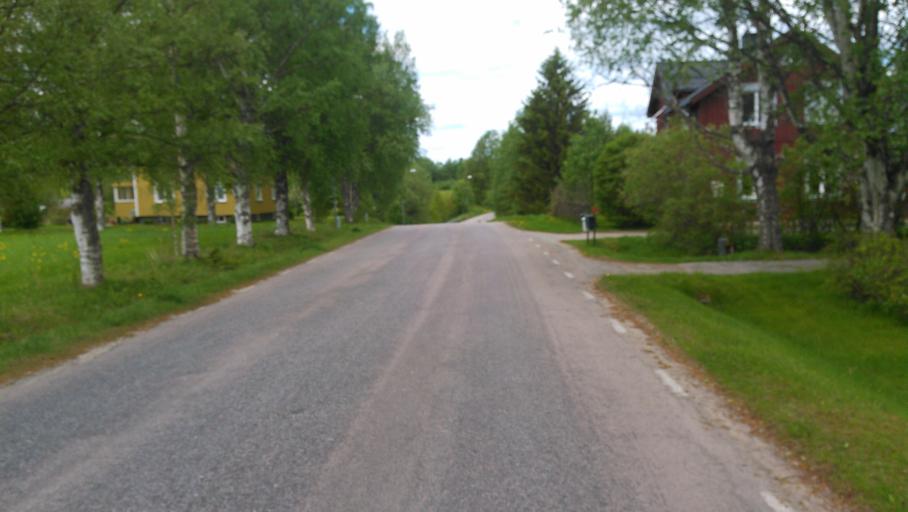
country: SE
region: Vaesterbotten
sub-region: Umea Kommun
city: Roback
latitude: 63.8691
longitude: 20.0692
